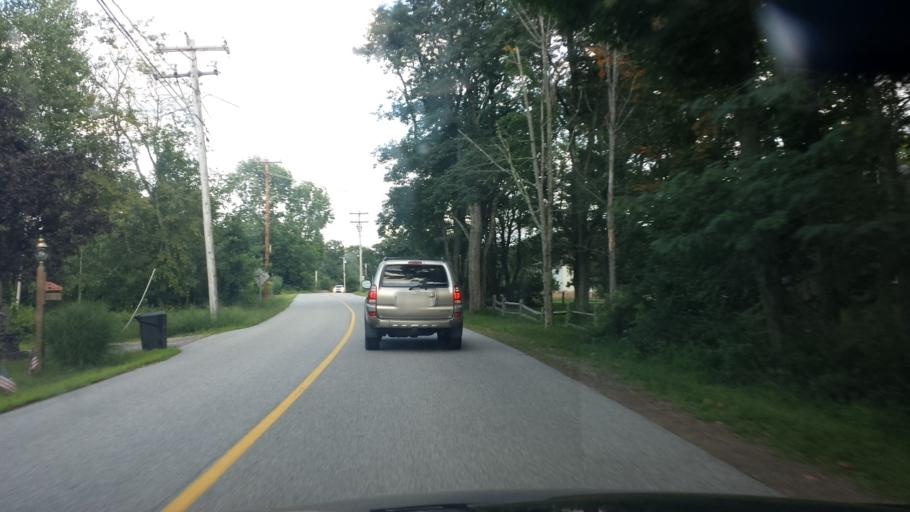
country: US
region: Maine
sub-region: York County
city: Arundel
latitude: 43.4299
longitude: -70.4548
